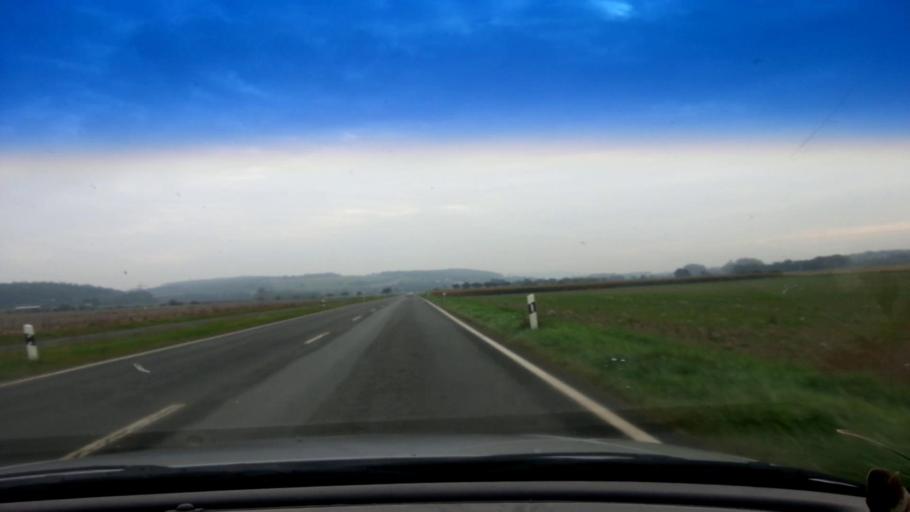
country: DE
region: Bavaria
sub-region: Upper Franconia
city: Ebensfeld
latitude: 50.0533
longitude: 10.9549
